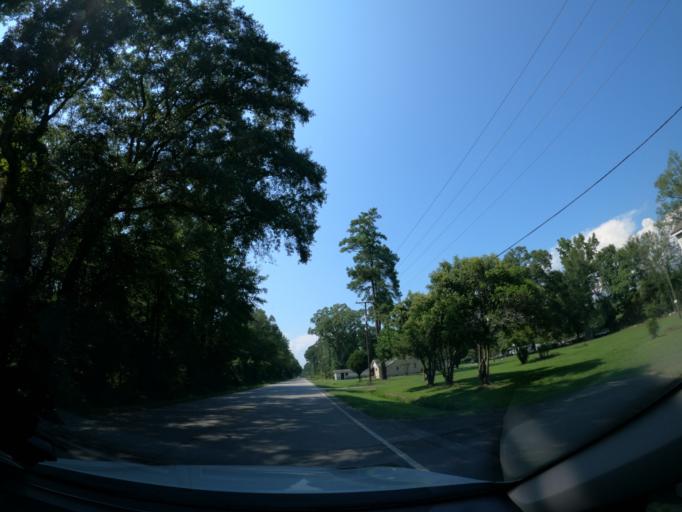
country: US
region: South Carolina
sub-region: Richland County
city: Hopkins
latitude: 33.8951
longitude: -80.9196
